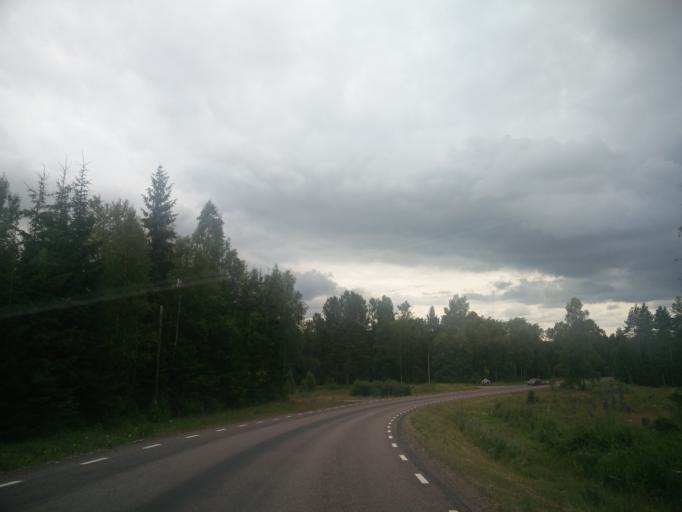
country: SE
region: Vaermland
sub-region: Arvika Kommun
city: Arvika
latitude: 59.9443
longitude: 12.6903
